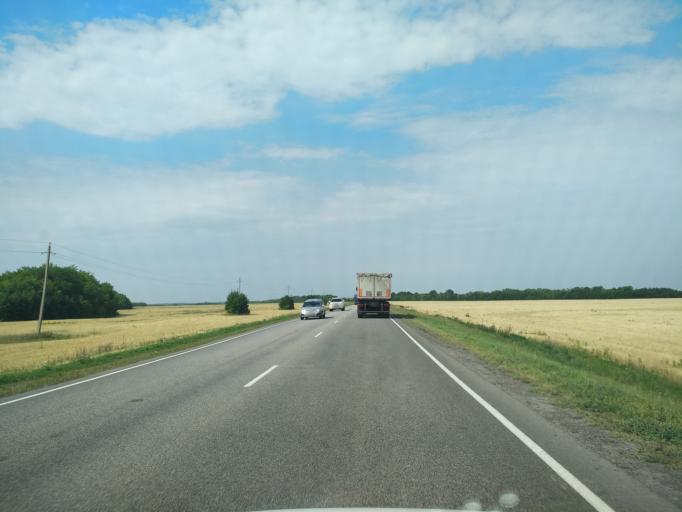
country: RU
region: Voronezj
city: Orlovo
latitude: 51.6778
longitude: 39.7816
